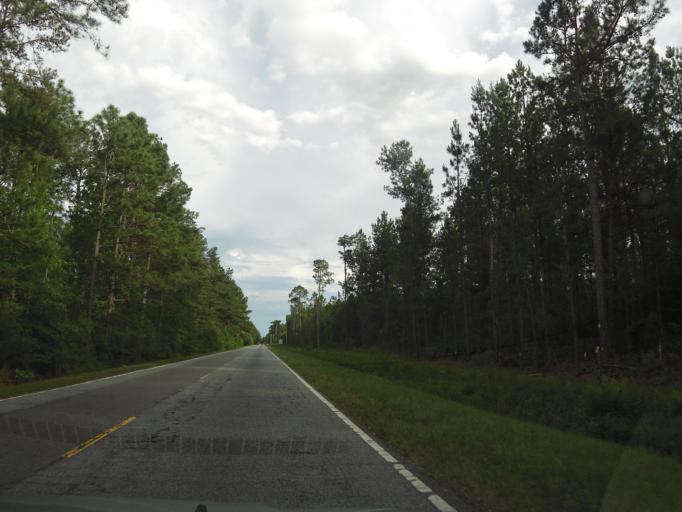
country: US
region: South Carolina
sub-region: Hampton County
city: Estill
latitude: 32.5634
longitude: -81.1778
